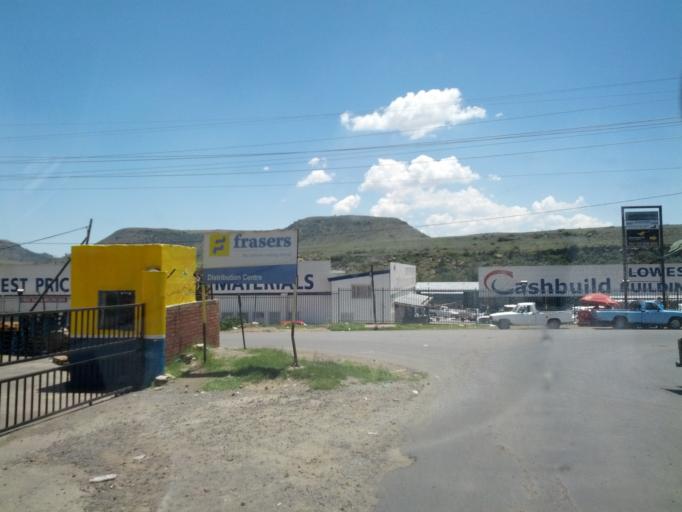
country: LS
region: Maseru
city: Maseru
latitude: -29.2978
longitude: 27.4767
